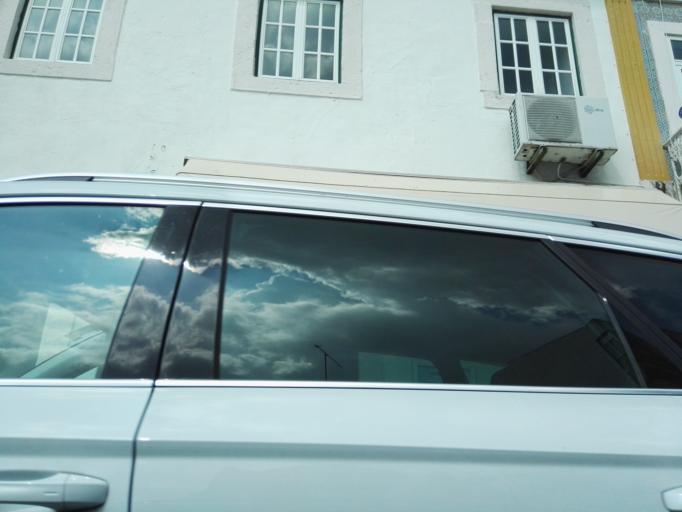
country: PT
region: Lisbon
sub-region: Vila Franca de Xira
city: Alhandra
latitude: 38.9260
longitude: -9.0070
